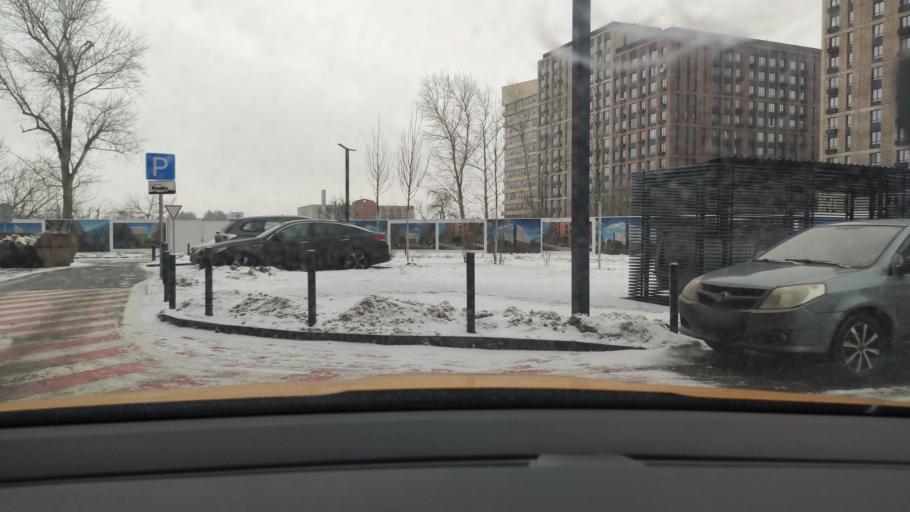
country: RU
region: Moscow
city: Orekhovo-Borisovo
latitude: 55.6007
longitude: 37.7276
